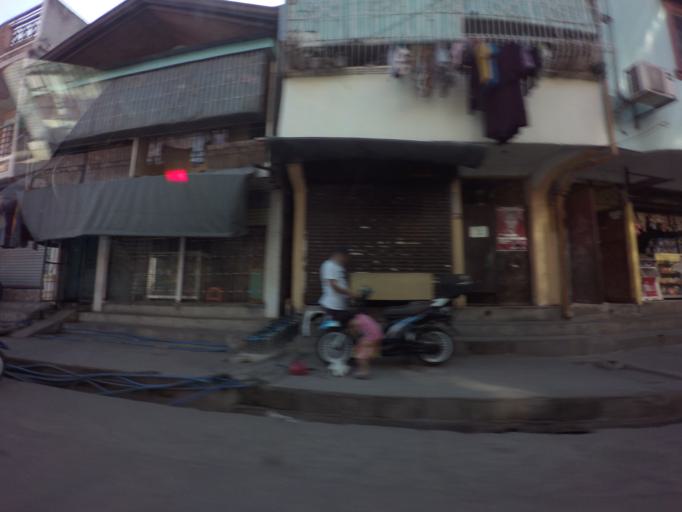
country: PH
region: Calabarzon
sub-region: Province of Rizal
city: Taguig
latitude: 14.4958
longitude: 121.0566
